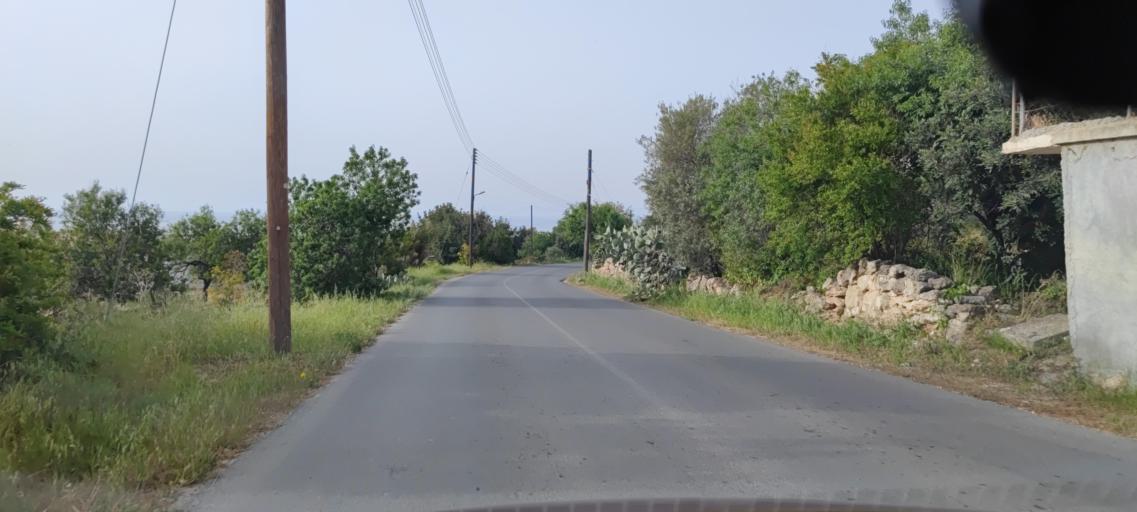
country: CY
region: Ammochostos
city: Leonarisso
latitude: 35.5377
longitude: 34.1933
